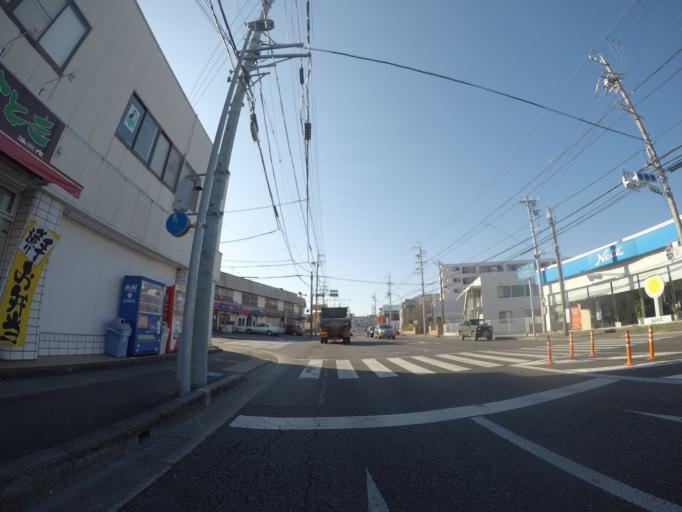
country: JP
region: Shizuoka
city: Shizuoka-shi
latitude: 34.9876
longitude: 138.4244
